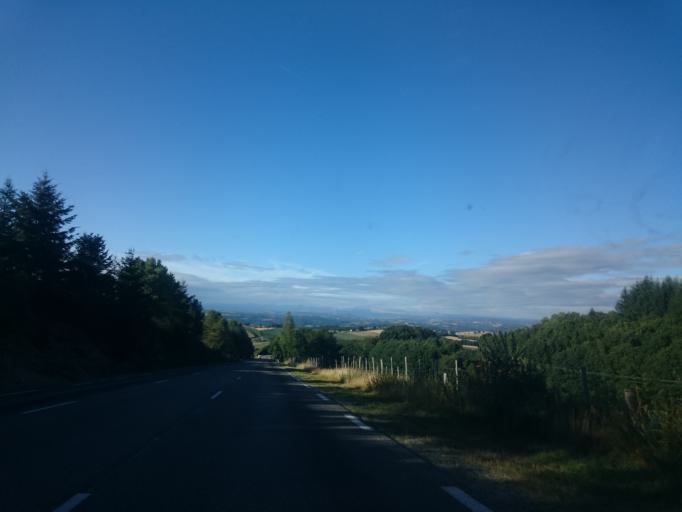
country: FR
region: Midi-Pyrenees
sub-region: Departement de l'Aveyron
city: Entraygues-sur-Truyere
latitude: 44.7176
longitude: 2.5028
